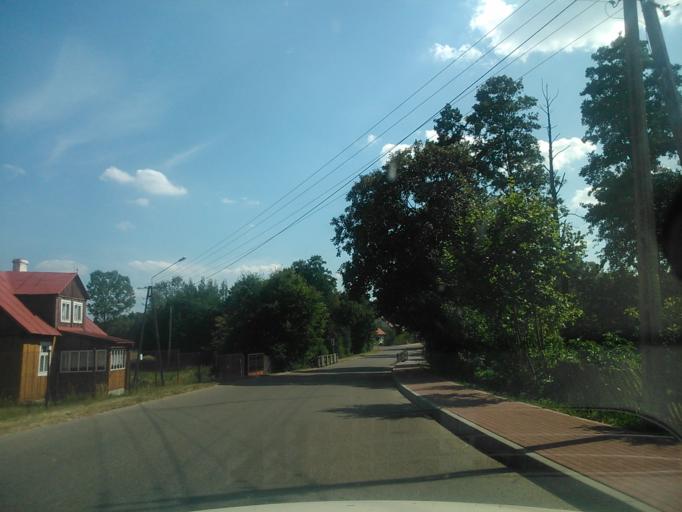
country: PL
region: Masovian Voivodeship
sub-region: Powiat ostrolecki
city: Czarnia
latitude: 53.3552
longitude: 21.2017
